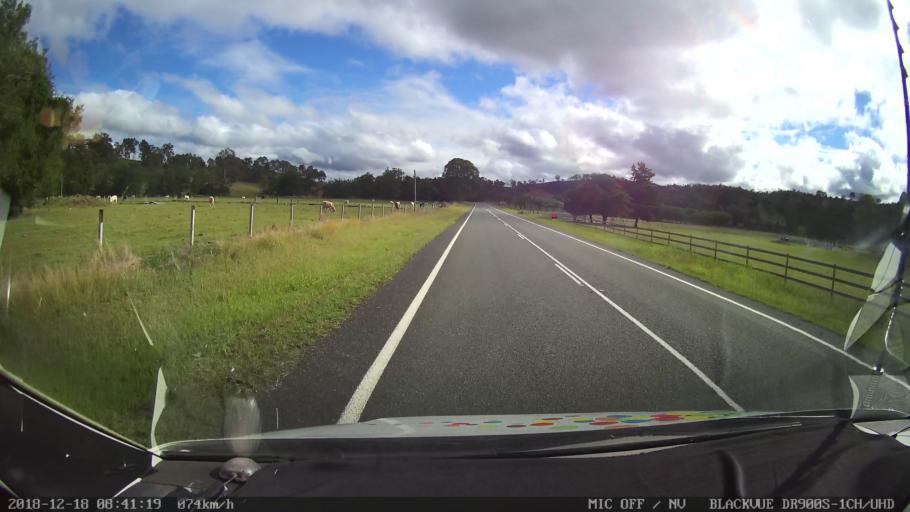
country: AU
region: Queensland
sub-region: Logan
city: Cedar Vale
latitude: -28.2376
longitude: 152.8561
